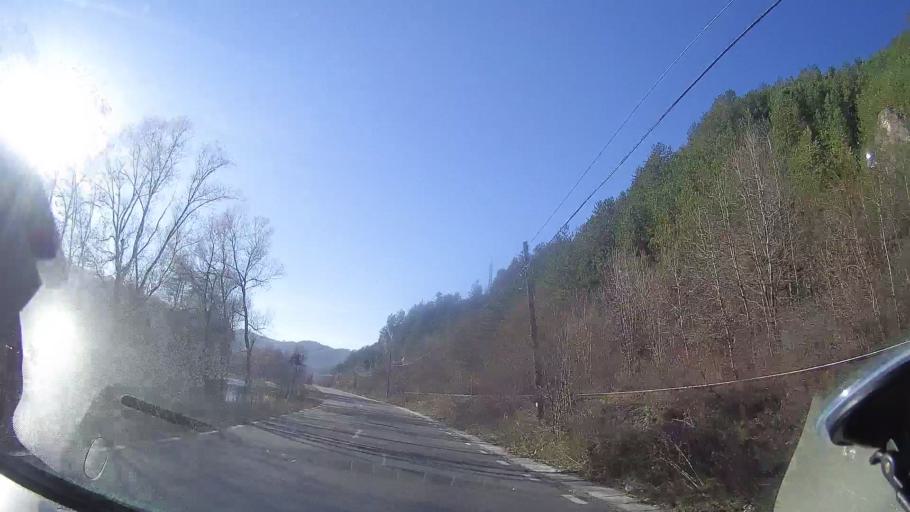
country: RO
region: Bihor
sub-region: Comuna Bratca
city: Bratca
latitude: 46.9295
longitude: 22.6342
